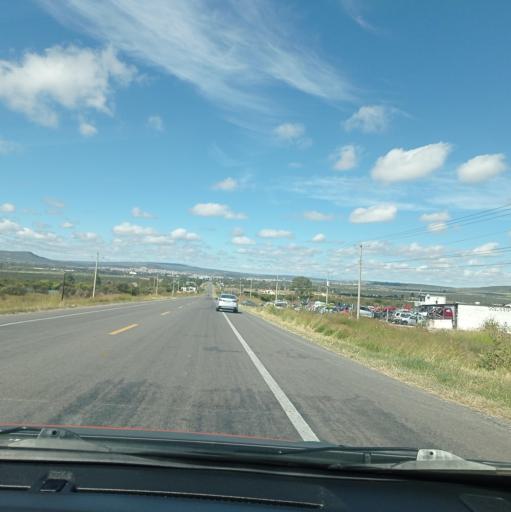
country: MX
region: Jalisco
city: San Miguel el Alto
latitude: 21.0173
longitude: -102.3352
